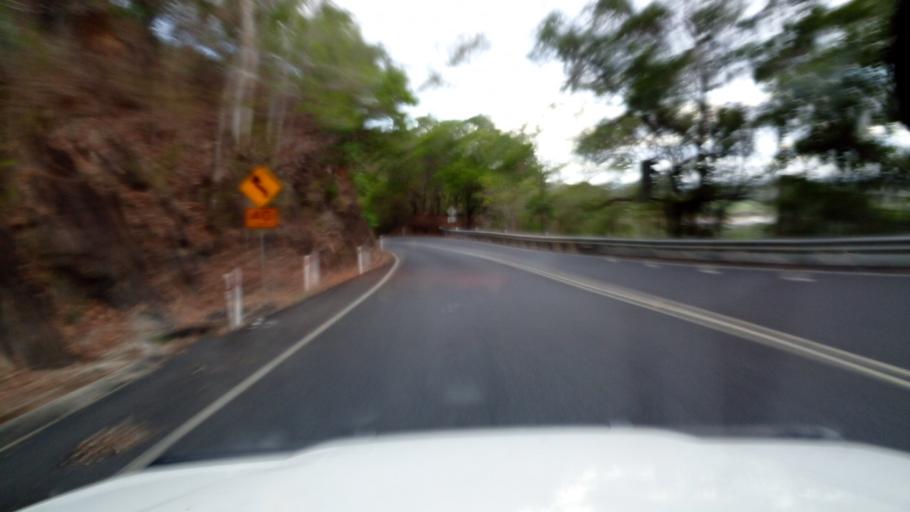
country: AU
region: Queensland
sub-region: Cairns
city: Redlynch
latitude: -16.8419
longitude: 145.6815
